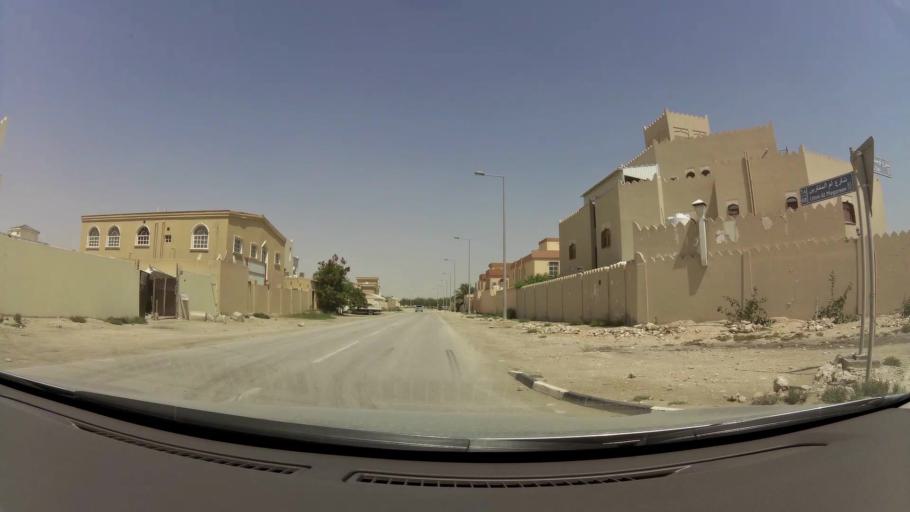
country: QA
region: Baladiyat Umm Salal
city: Umm Salal Muhammad
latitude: 25.3775
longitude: 51.4756
